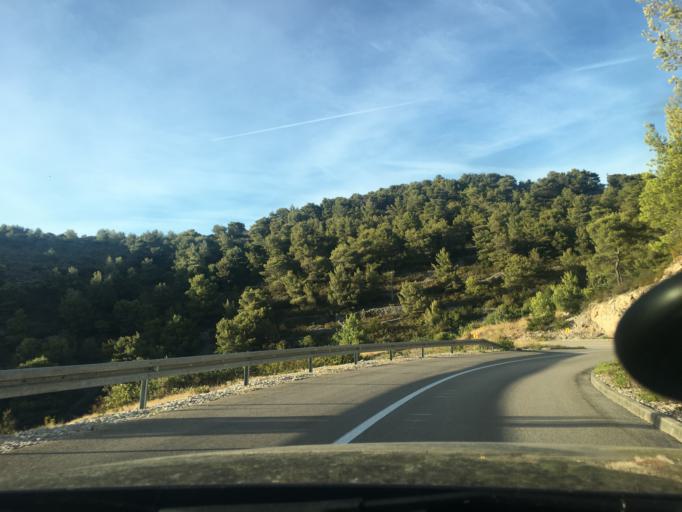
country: HR
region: Splitsko-Dalmatinska
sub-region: Grad Vis
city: Vis
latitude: 43.0581
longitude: 16.2059
